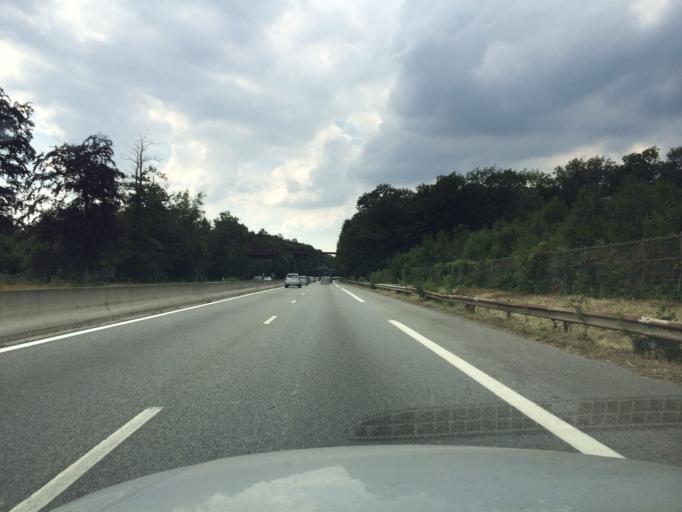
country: FR
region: Ile-de-France
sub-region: Departement des Yvelines
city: Bailly
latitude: 48.8473
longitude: 2.0783
